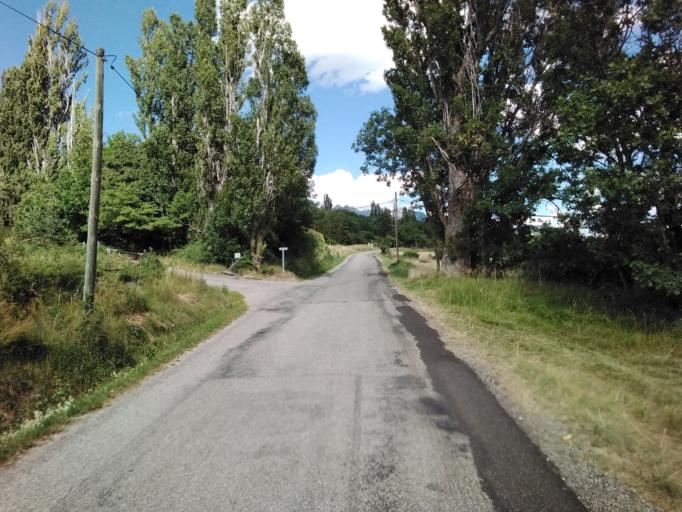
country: FR
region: Provence-Alpes-Cote d'Azur
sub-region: Departement des Hautes-Alpes
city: La Batie-Neuve
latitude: 44.5876
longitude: 6.1483
